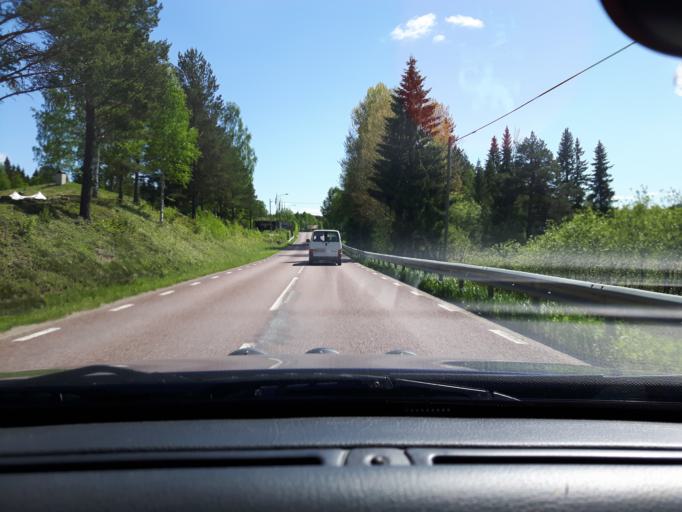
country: SE
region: Jaemtland
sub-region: Harjedalens Kommun
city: Sveg
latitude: 62.2959
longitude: 14.7842
